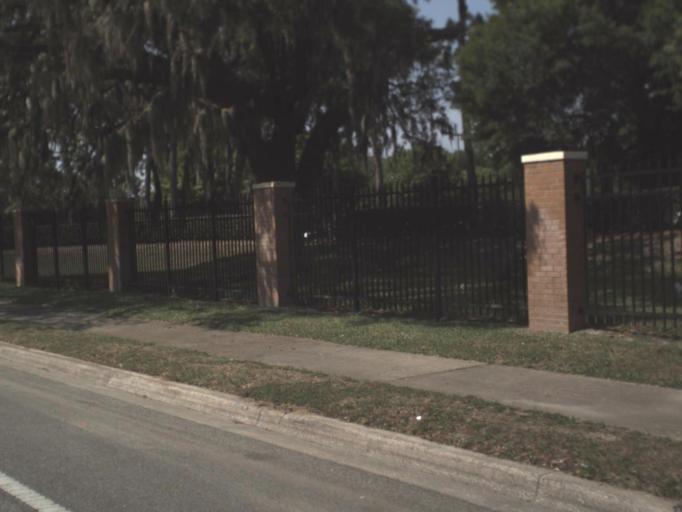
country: US
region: Florida
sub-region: Duval County
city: Jacksonville
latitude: 30.3541
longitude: -81.6033
